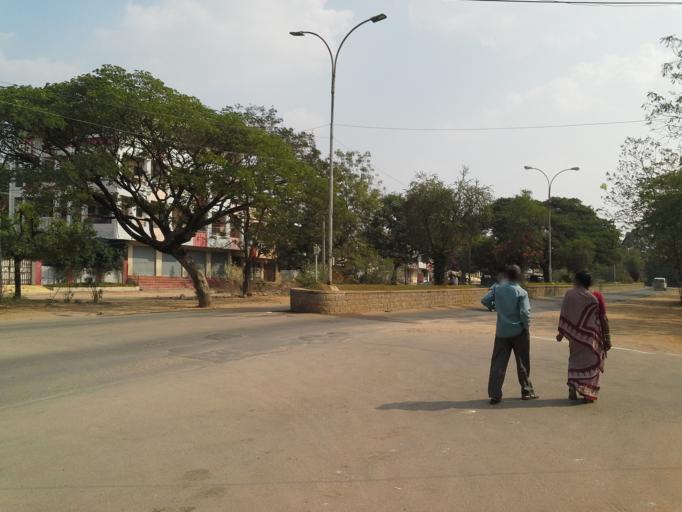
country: IN
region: Telangana
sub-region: Hyderabad
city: Hyderabad
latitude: 17.3181
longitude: 78.4034
